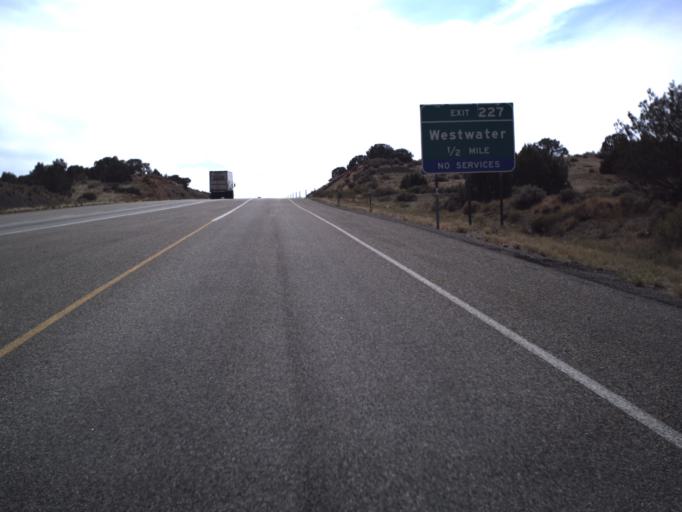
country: US
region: Colorado
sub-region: Mesa County
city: Loma
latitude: 39.1845
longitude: -109.1185
